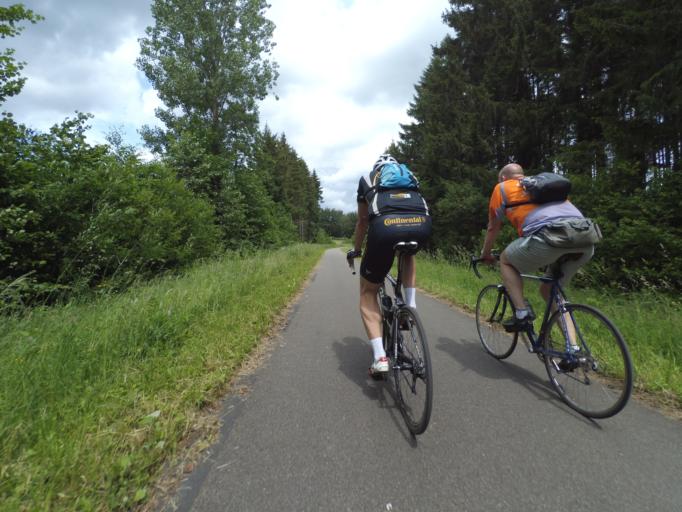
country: DE
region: North Rhine-Westphalia
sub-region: Regierungsbezirk Koln
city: Monschau
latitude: 50.5715
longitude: 6.2362
